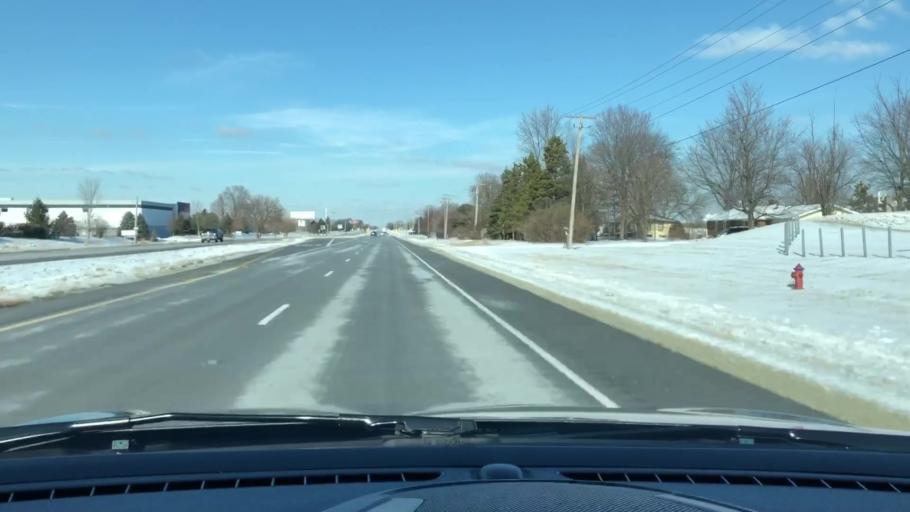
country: US
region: Illinois
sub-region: Will County
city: Preston Heights
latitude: 41.4610
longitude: -88.0793
